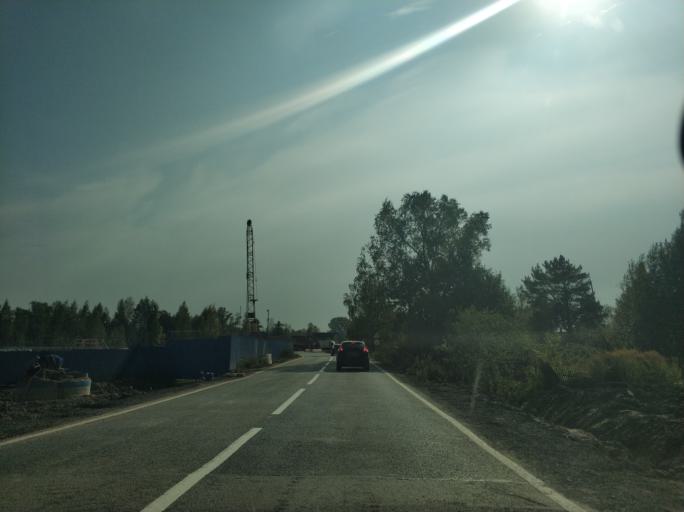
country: RU
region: St.-Petersburg
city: Krasnogvargeisky
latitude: 60.0082
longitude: 30.4859
